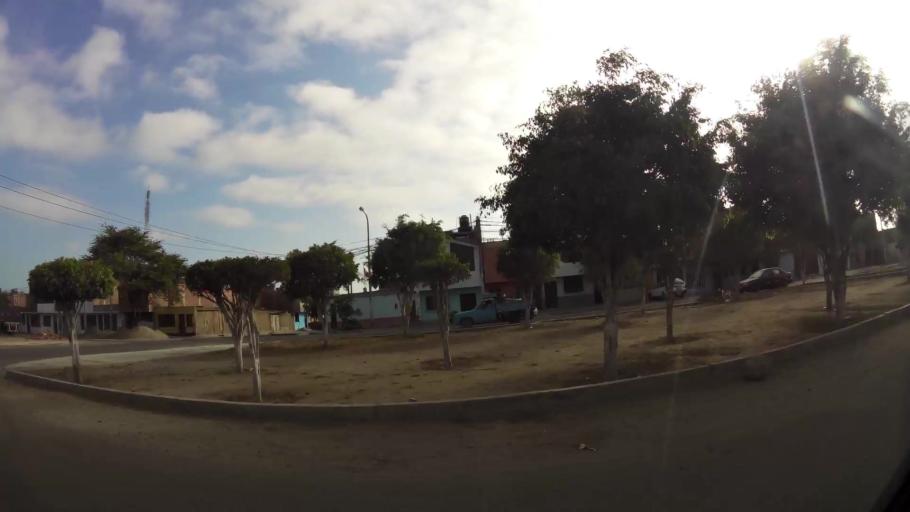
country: PE
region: La Libertad
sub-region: Provincia de Trujillo
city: La Esperanza
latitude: -8.0853
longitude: -79.0401
